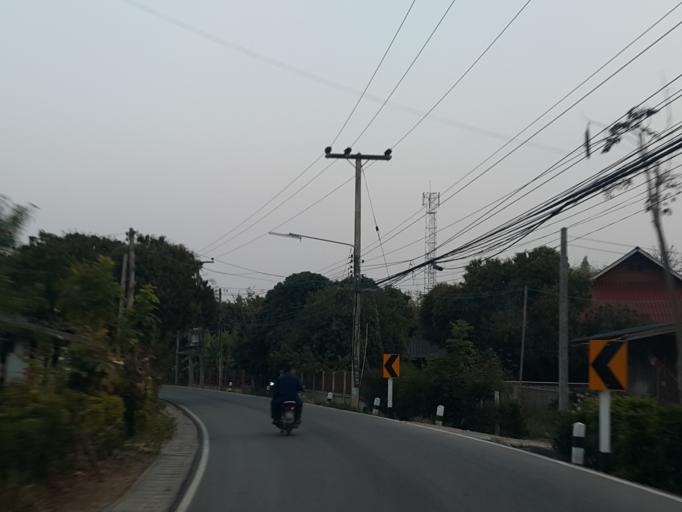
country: TH
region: Chiang Mai
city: Mae Taeng
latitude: 18.9934
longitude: 98.8922
